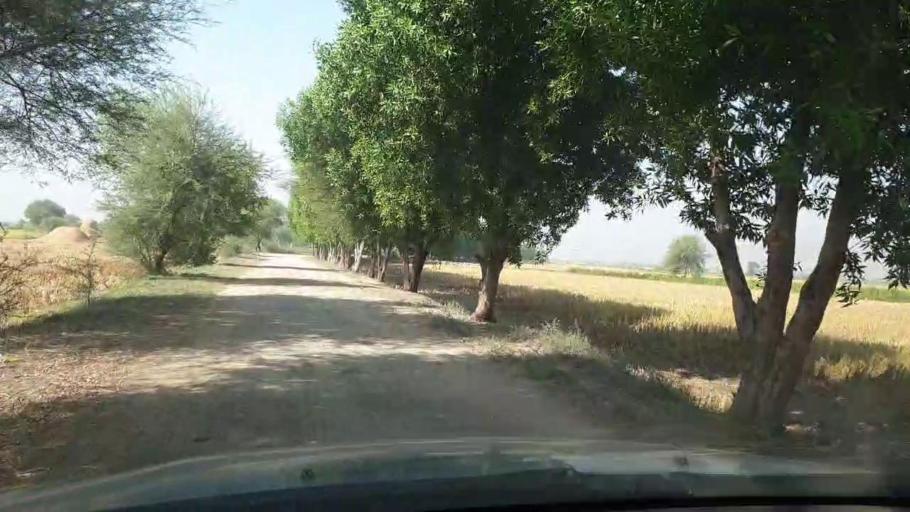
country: PK
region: Sindh
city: Bulri
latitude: 24.9004
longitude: 68.4214
